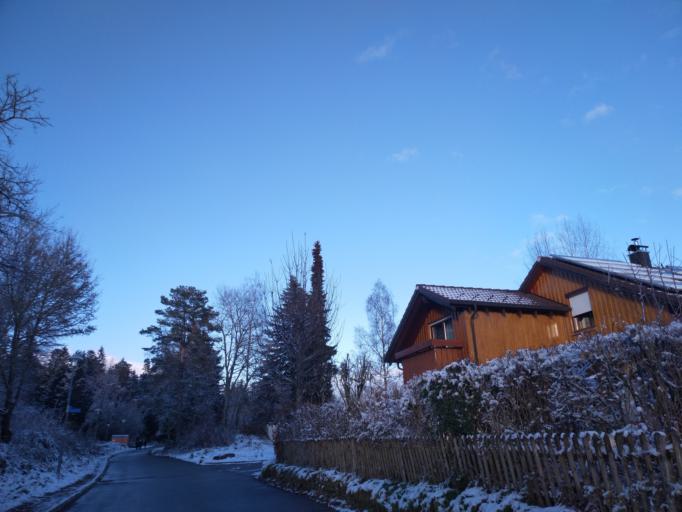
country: DE
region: Baden-Wuerttemberg
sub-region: Karlsruhe Region
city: Simmersfeld
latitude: 48.6241
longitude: 8.5069
